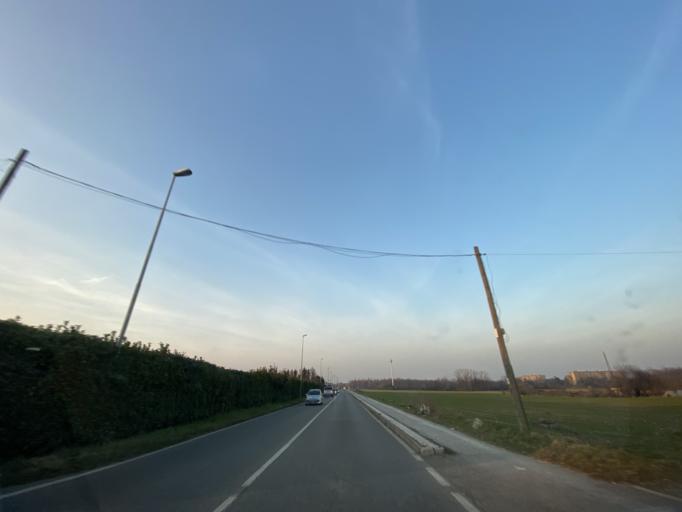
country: IT
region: Lombardy
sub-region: Citta metropolitana di Milano
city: Solaro
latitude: 45.6053
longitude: 9.0793
